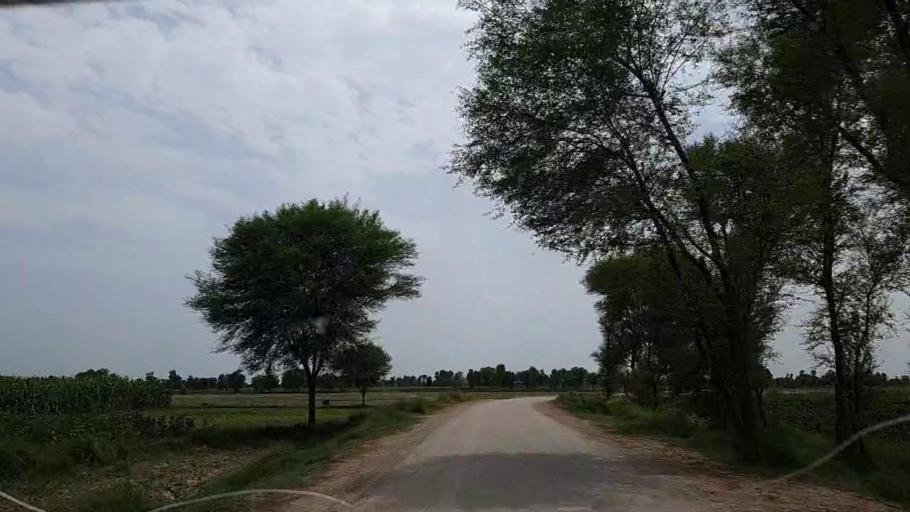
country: PK
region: Sindh
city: Tharu Shah
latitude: 26.9266
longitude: 68.1040
